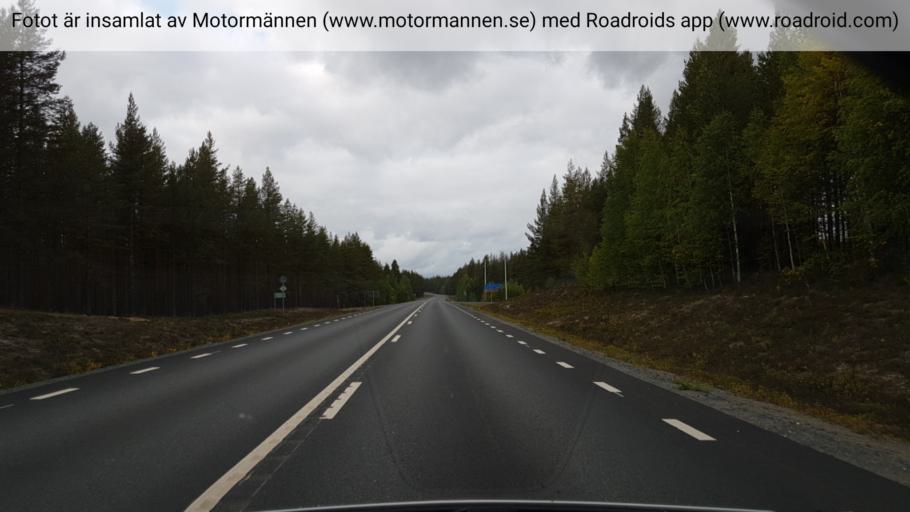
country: SE
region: Vaesterbotten
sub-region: Norsjo Kommun
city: Norsjoe
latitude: 64.9788
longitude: 19.6304
